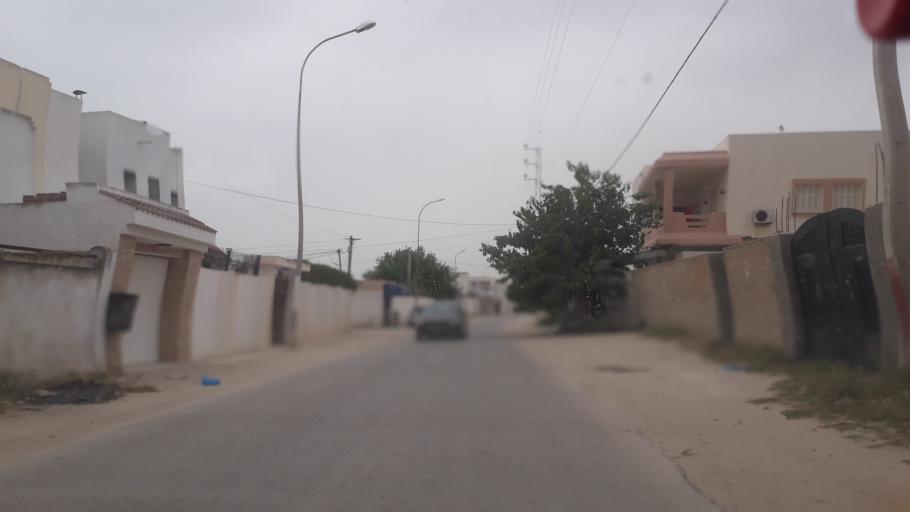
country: TN
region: Safaqis
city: Al Qarmadah
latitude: 34.7960
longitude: 10.7667
